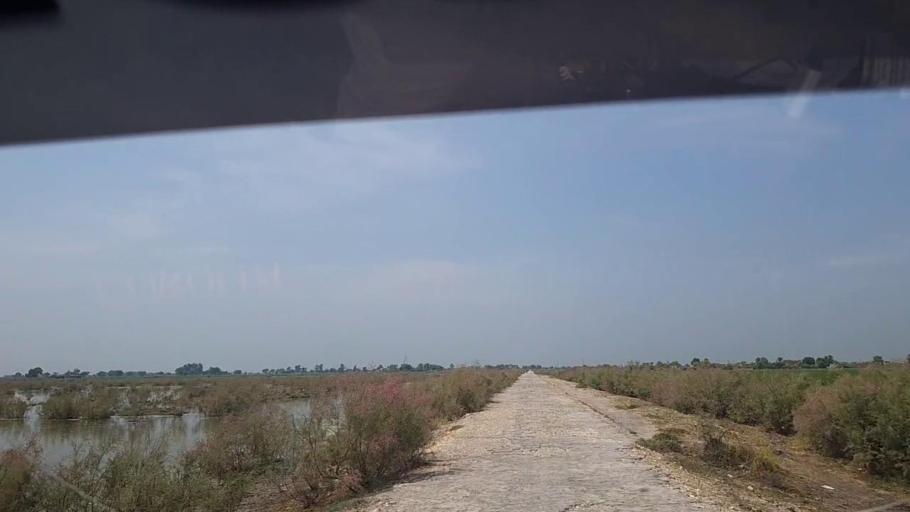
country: PK
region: Sindh
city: Thul
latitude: 28.1690
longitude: 68.7598
